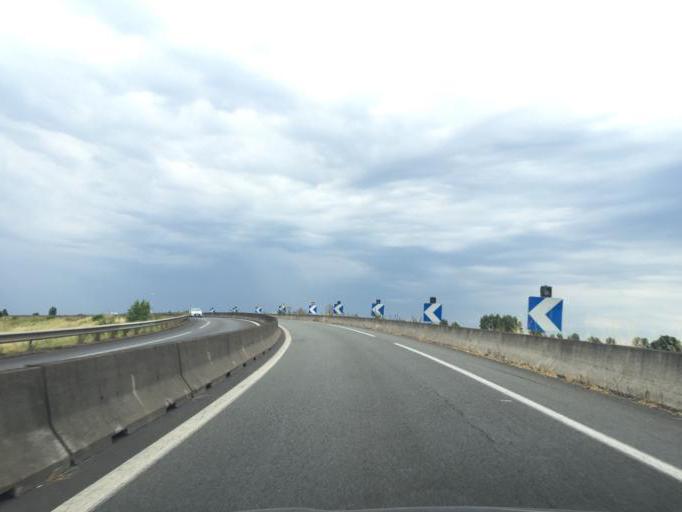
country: FR
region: Auvergne
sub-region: Departement de l'Allier
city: Toulon-sur-Allier
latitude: 46.5035
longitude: 3.3567
